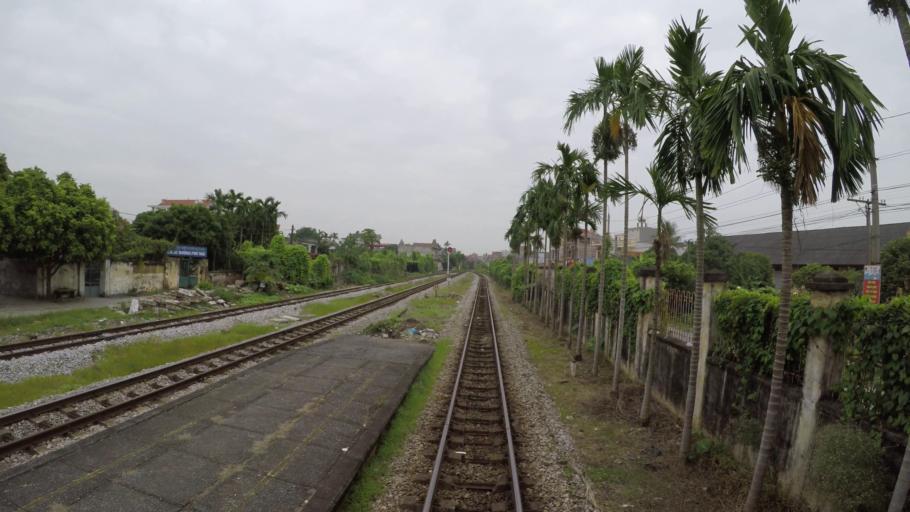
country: VN
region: Hai Duong
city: Phu Thai
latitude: 20.9722
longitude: 106.4911
